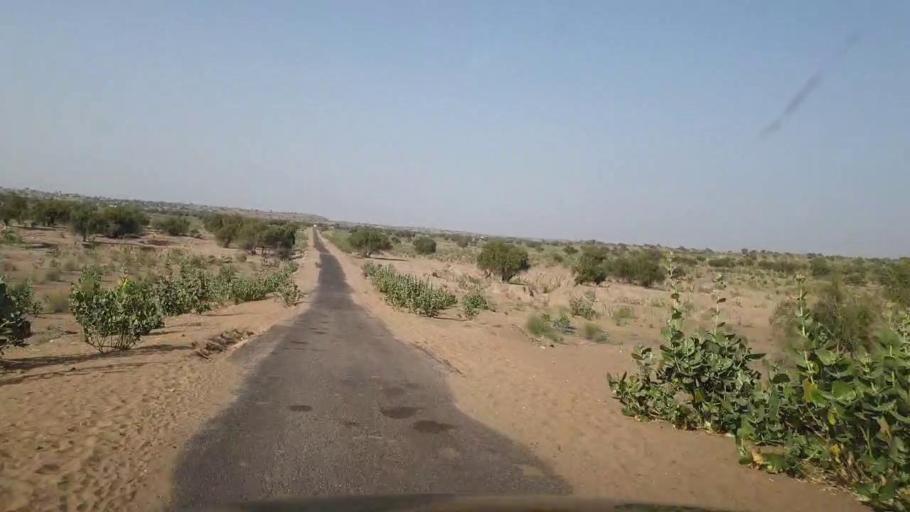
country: PK
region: Sindh
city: Islamkot
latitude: 25.1491
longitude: 70.5199
